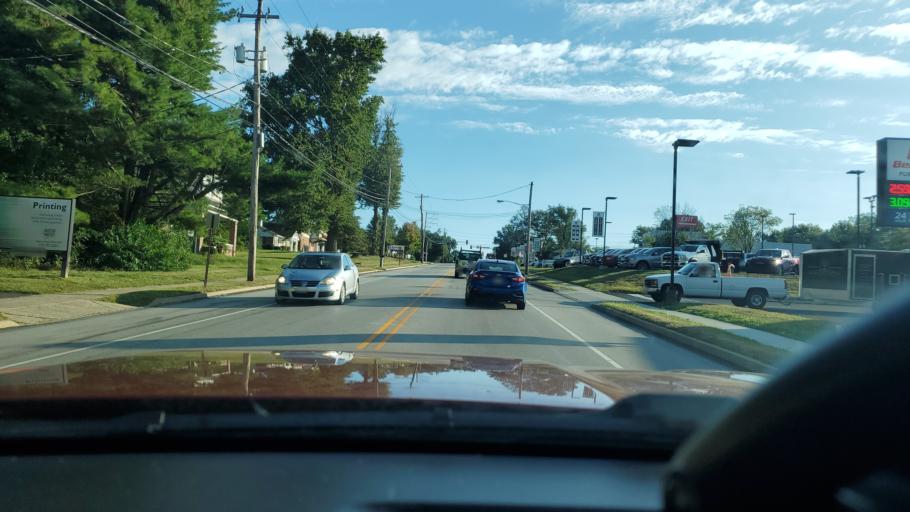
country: US
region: Pennsylvania
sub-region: Montgomery County
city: Telford
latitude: 40.3098
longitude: -75.3556
